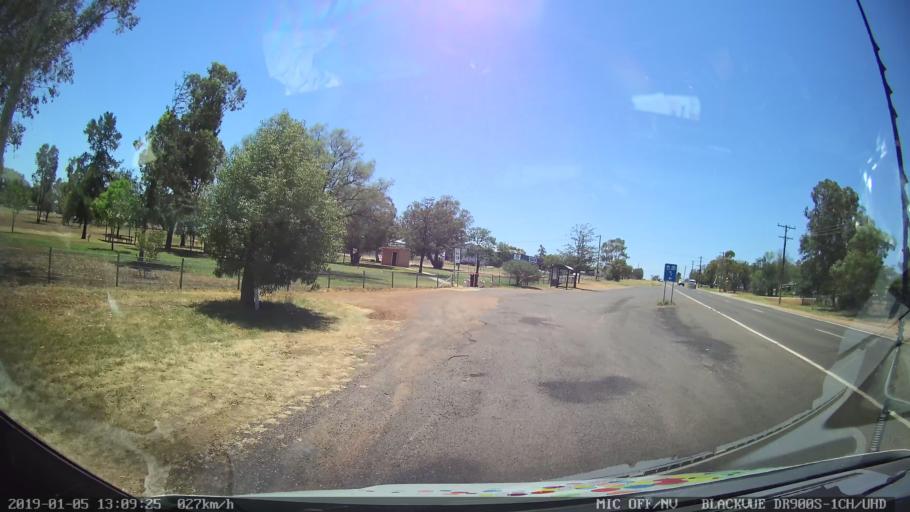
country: AU
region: New South Wales
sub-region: Gunnedah
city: Gunnedah
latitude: -31.0981
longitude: 149.9097
